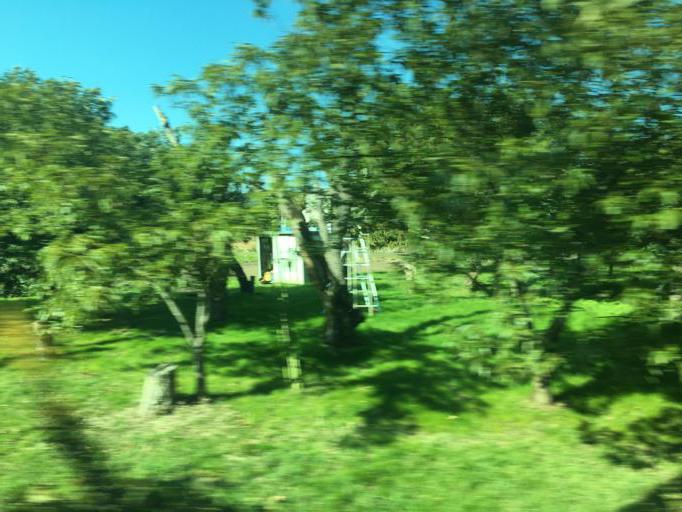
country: JP
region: Ibaraki
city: Iwase
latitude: 36.3573
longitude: 140.0957
